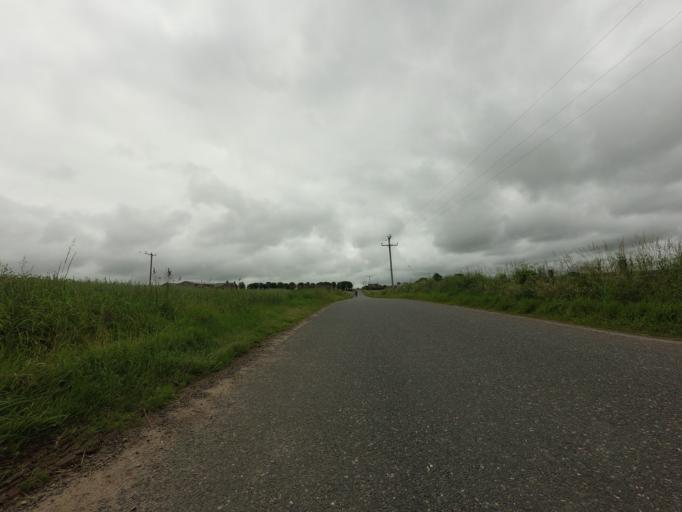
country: GB
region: Scotland
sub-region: Aberdeenshire
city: Turriff
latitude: 57.5355
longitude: -2.4348
